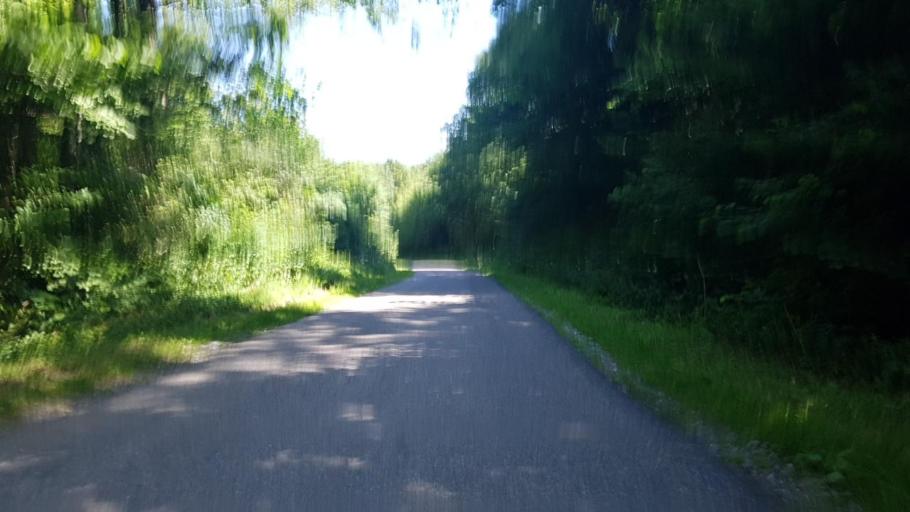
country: BE
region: Wallonia
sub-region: Province du Hainaut
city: Momignies
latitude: 50.0816
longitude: 4.2282
